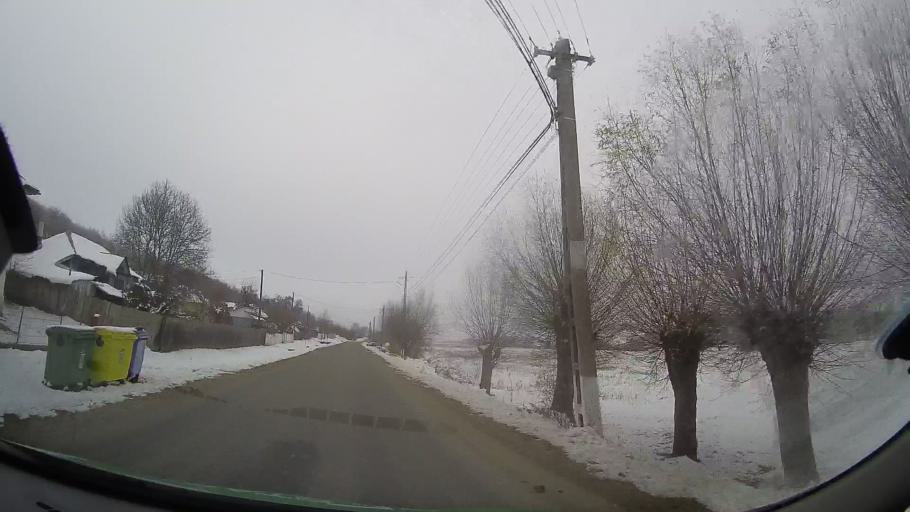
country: RO
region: Bacau
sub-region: Comuna Vultureni
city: Vultureni
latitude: 46.3261
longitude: 27.2918
